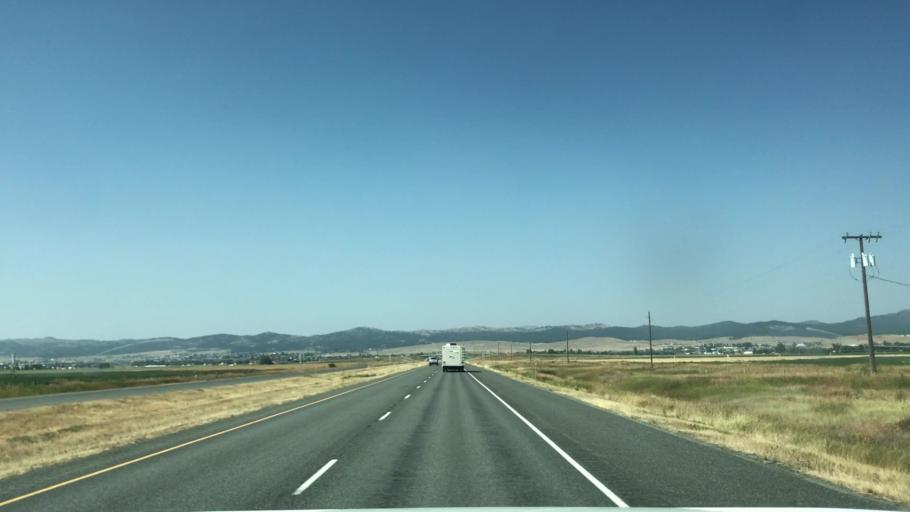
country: US
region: Montana
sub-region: Lewis and Clark County
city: Helena Valley West Central
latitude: 46.6930
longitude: -112.0117
